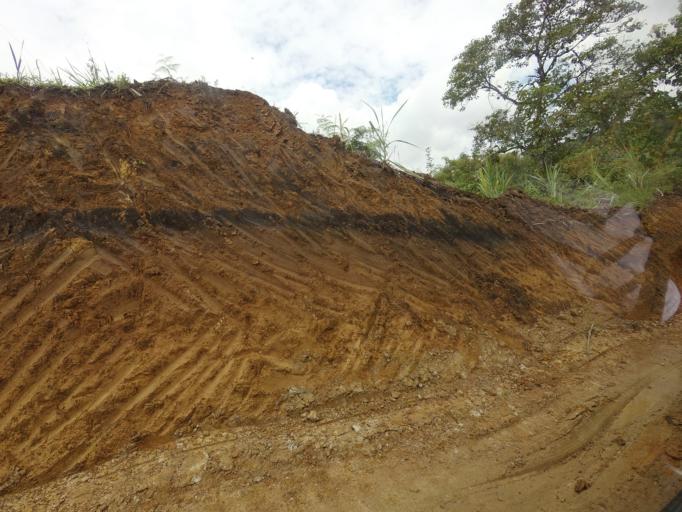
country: CO
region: Huila
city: Isnos
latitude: 1.9555
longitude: -76.2899
